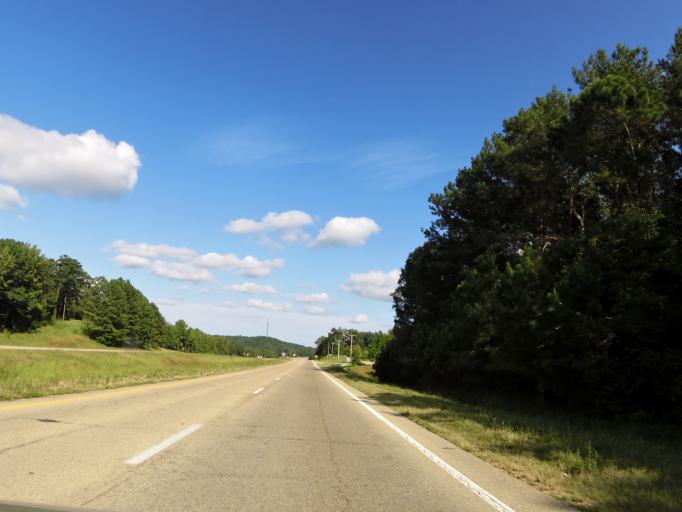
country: US
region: Mississippi
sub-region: Alcorn County
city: Farmington
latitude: 34.8530
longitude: -88.3577
